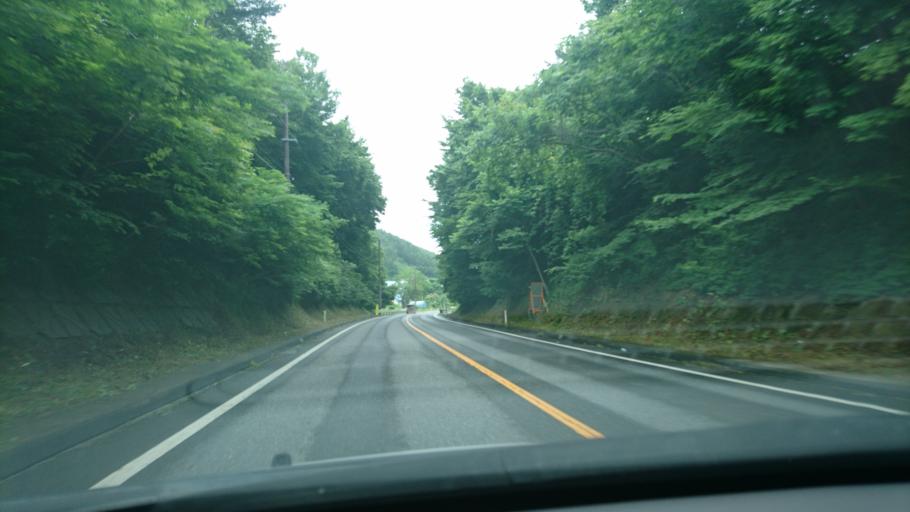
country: JP
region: Iwate
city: Yamada
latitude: 39.4045
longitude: 141.9558
